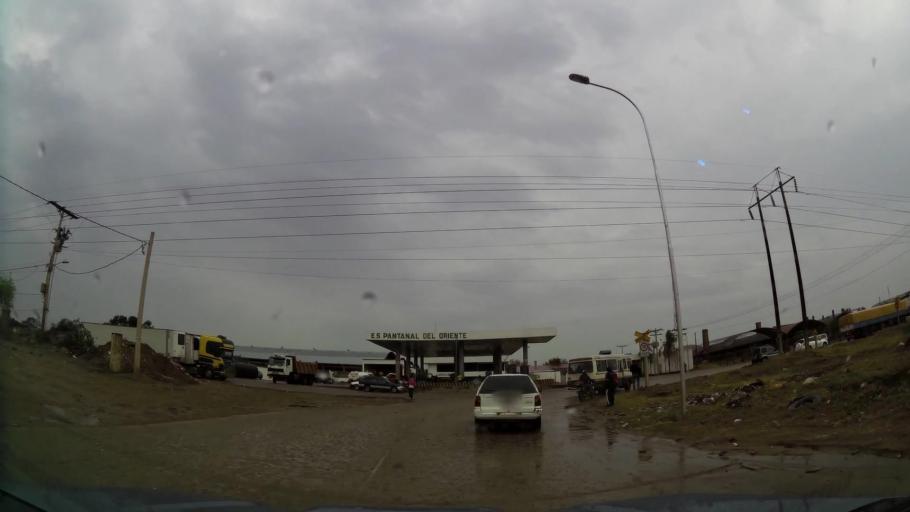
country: BO
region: Santa Cruz
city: Santa Cruz de la Sierra
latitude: -17.7567
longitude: -63.1323
